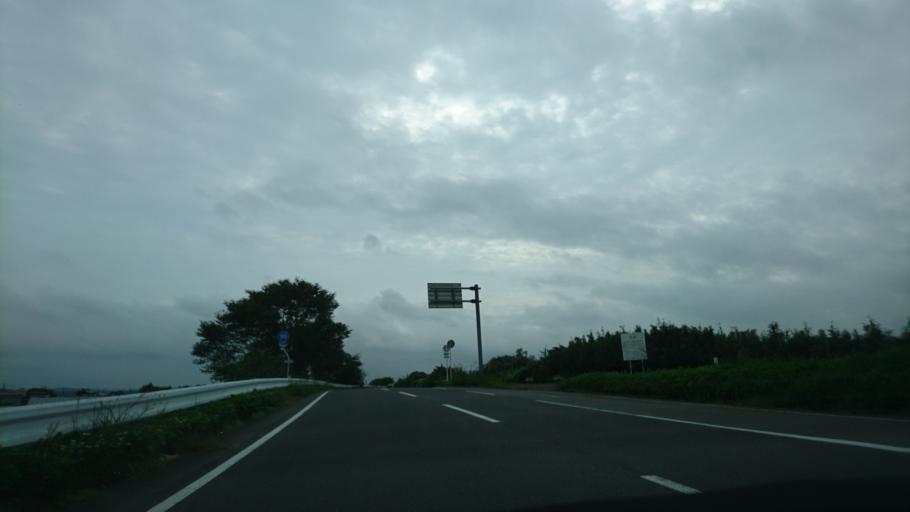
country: JP
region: Iwate
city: Ichinoseki
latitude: 38.7804
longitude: 141.1164
